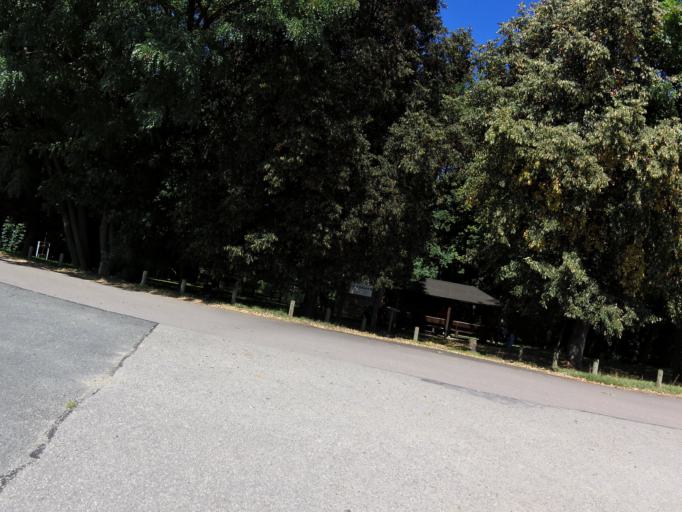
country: DE
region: Saxony
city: Beilrode
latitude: 51.5179
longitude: 13.0505
